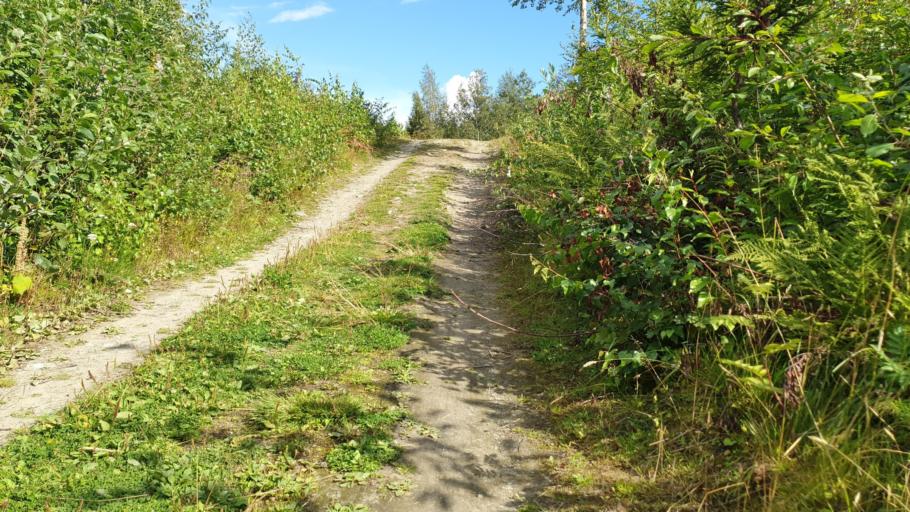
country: NO
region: Nord-Trondelag
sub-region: Levanger
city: Levanger
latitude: 63.7716
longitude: 11.3691
